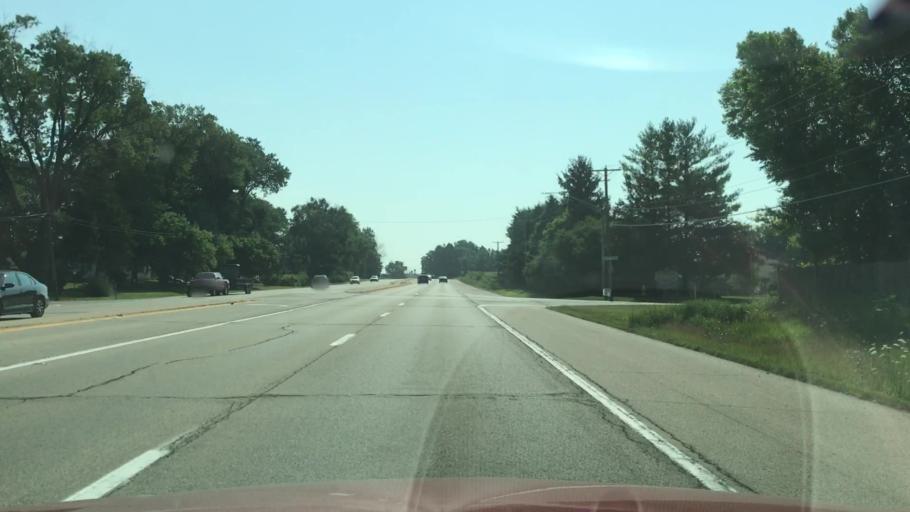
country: US
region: Illinois
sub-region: Winnebago County
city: Cherry Valley
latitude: 42.2385
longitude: -88.9891
